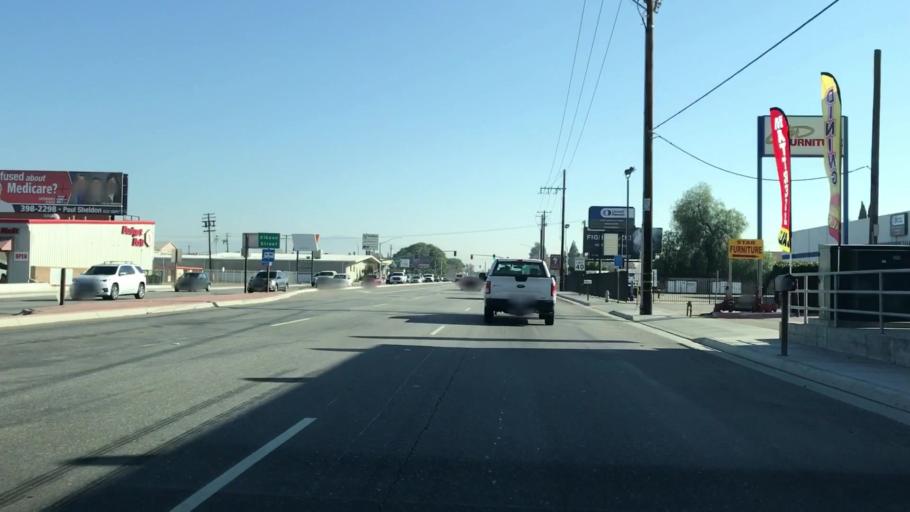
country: US
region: California
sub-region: Kern County
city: Bakersfield
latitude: 35.3832
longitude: -119.0544
